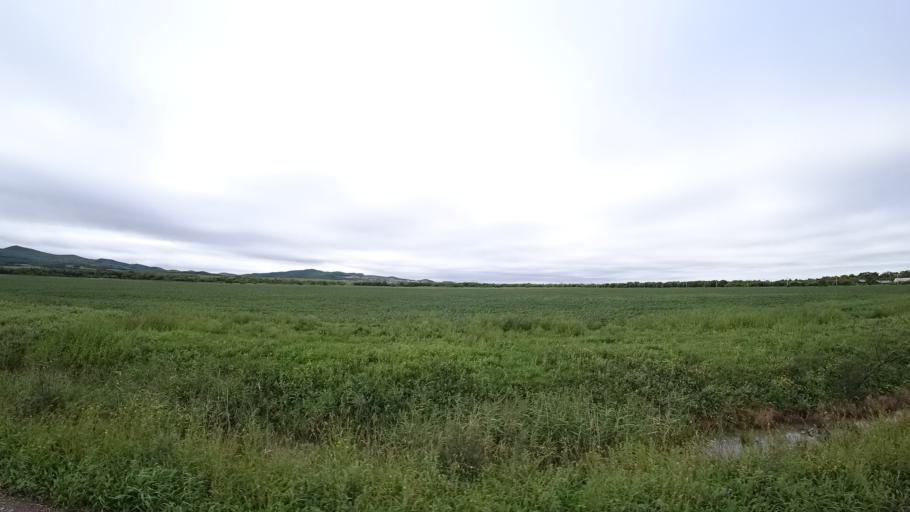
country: RU
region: Primorskiy
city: Monastyrishche
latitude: 44.1812
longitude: 132.4842
